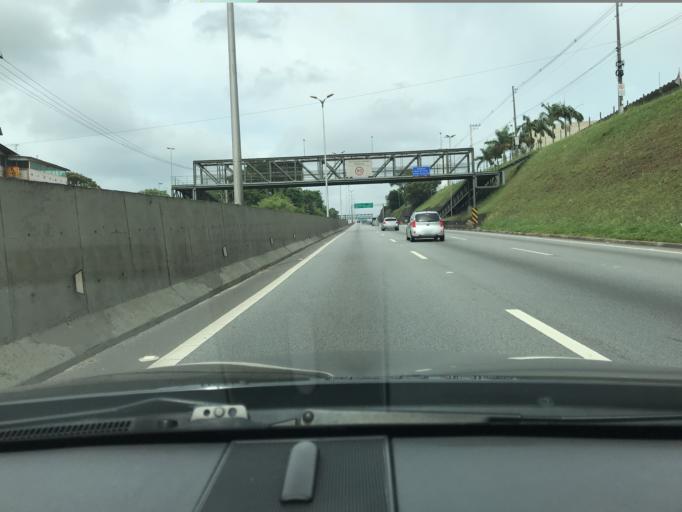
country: BR
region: Sao Paulo
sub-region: Cotia
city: Cotia
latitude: -23.5996
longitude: -46.8973
